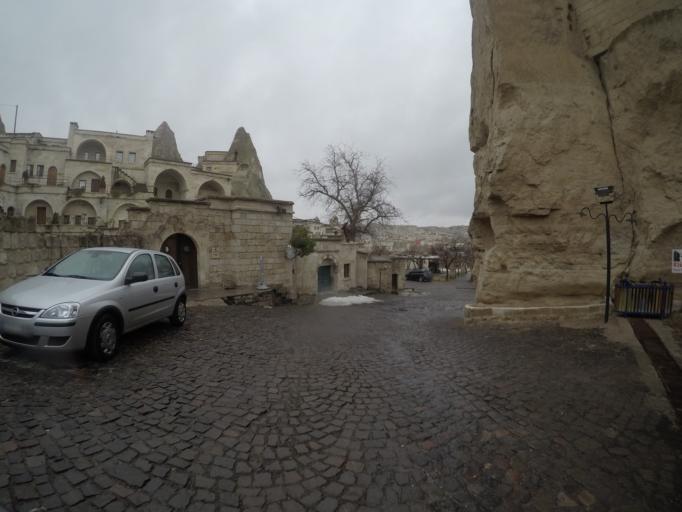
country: TR
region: Nevsehir
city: Goereme
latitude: 38.6423
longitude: 34.8321
